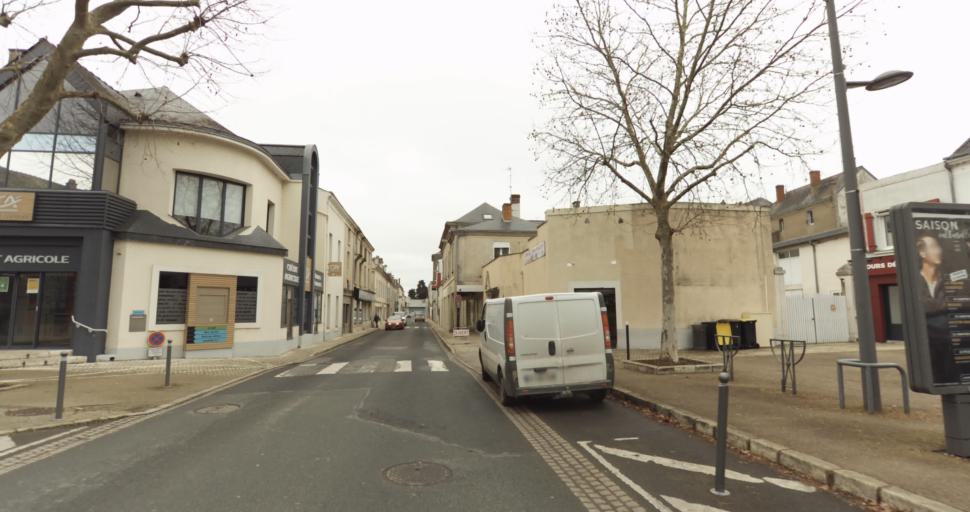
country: FR
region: Pays de la Loire
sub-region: Departement de Maine-et-Loire
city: Doue-la-Fontaine
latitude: 47.1928
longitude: -0.2761
